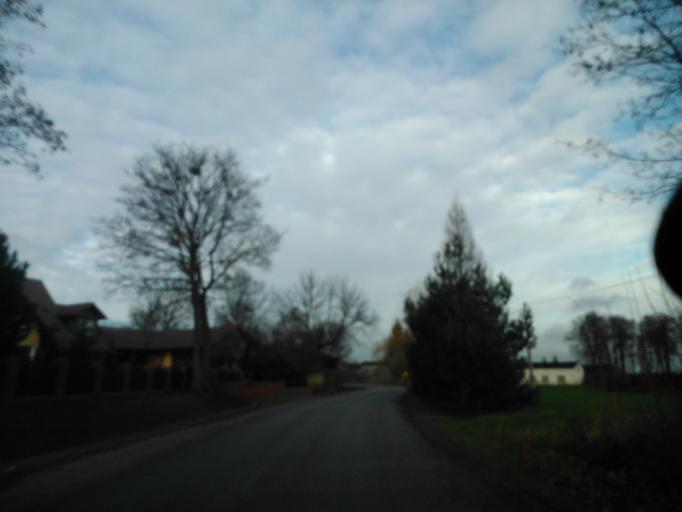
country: PL
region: Kujawsko-Pomorskie
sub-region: Powiat wabrzeski
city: Debowa Laka
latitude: 53.2157
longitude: 19.1195
